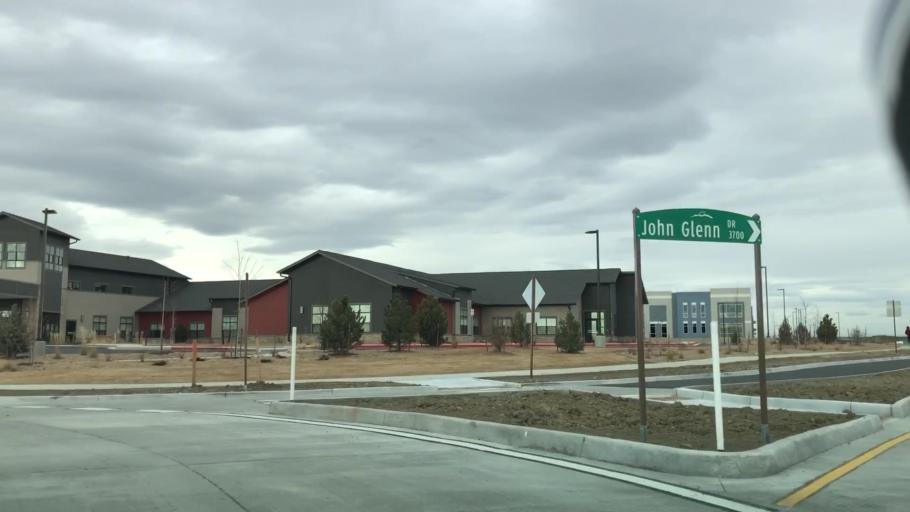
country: US
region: Colorado
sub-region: Larimer County
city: Loveland
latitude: 40.4290
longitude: -105.0099
